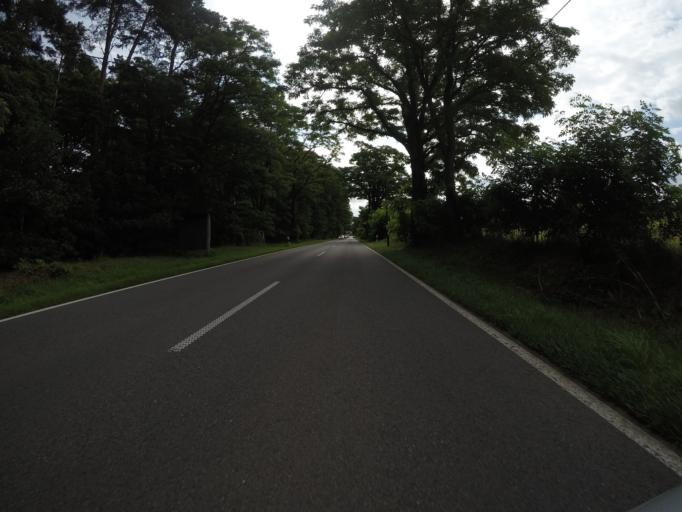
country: DE
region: Brandenburg
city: Grosswoltersdorf
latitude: 53.1043
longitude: 13.0386
